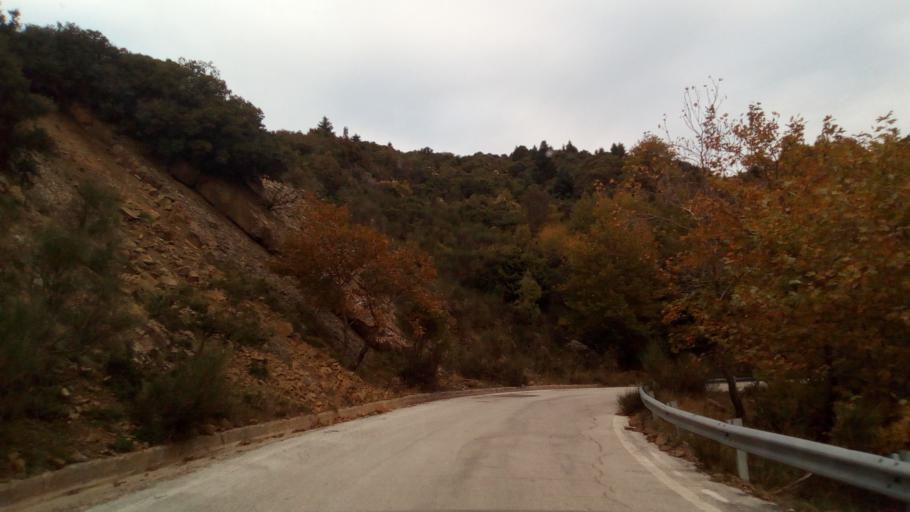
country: GR
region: West Greece
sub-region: Nomos Aitolias kai Akarnanias
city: Thermo
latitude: 38.6053
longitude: 21.7982
